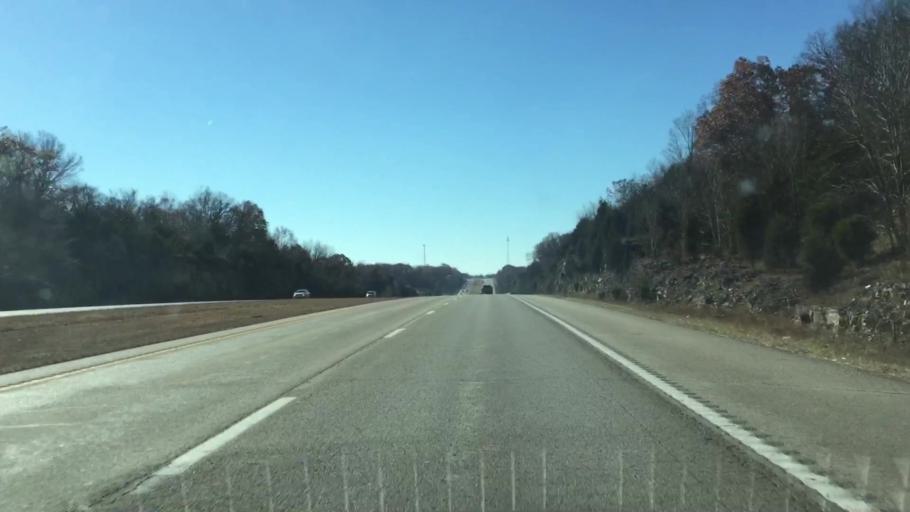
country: US
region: Missouri
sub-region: Cole County
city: Wardsville
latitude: 38.4971
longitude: -92.2684
